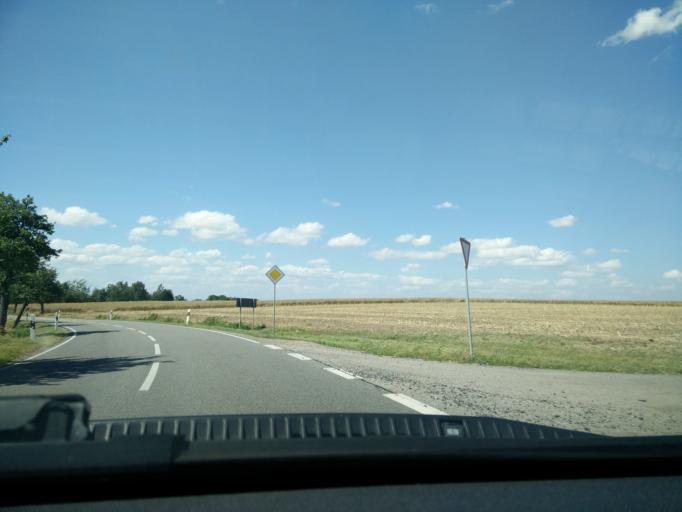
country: DE
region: Saxony
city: Geithain
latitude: 51.0471
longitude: 12.7165
